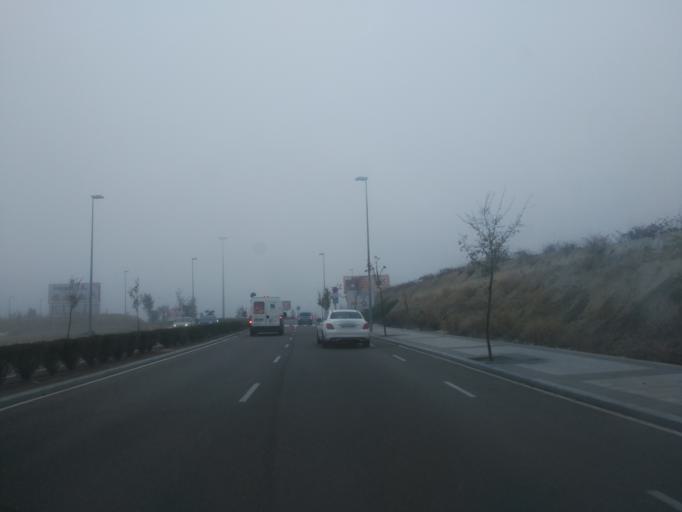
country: ES
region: Castille and Leon
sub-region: Provincia de Valladolid
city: Zaratan
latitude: 41.6346
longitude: -4.7844
